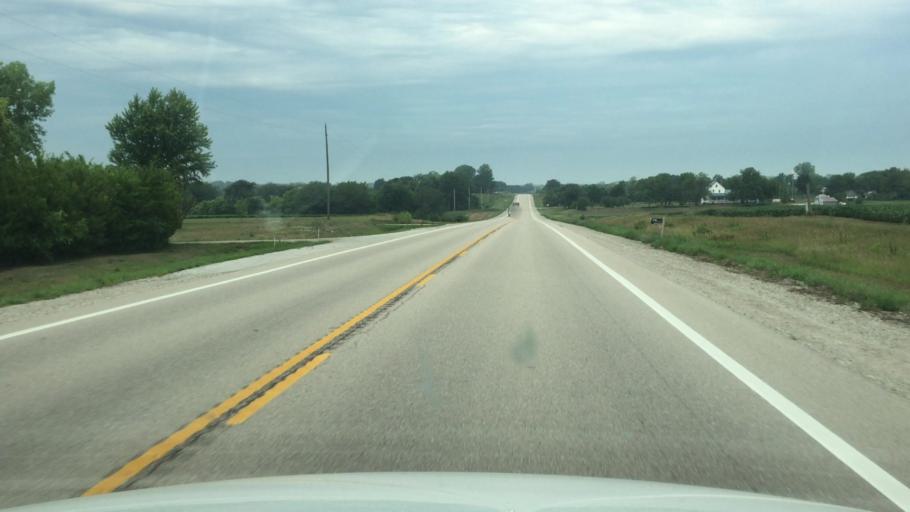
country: US
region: Kansas
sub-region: Brown County
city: Hiawatha
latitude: 39.8484
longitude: -95.6532
